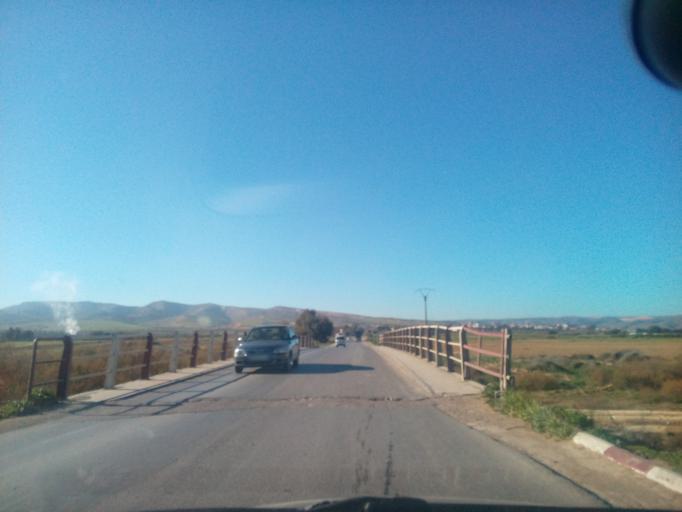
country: DZ
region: Relizane
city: Relizane
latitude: 35.8989
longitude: 0.5376
